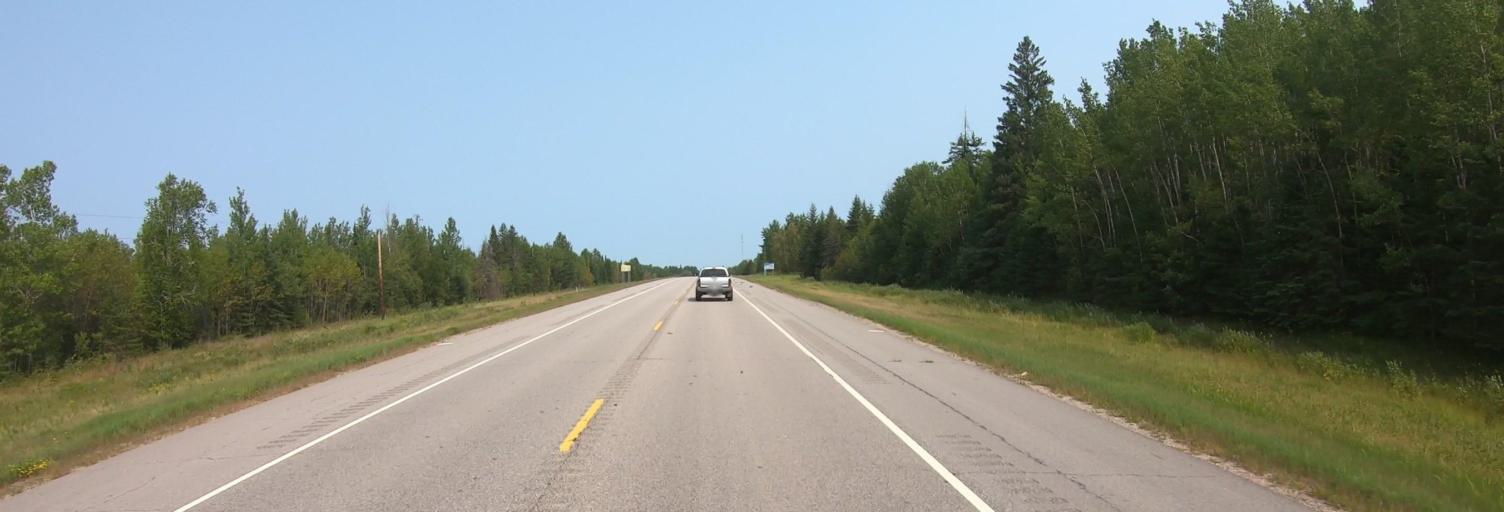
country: CA
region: Ontario
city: Fort Frances
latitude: 48.3329
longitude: -92.9630
